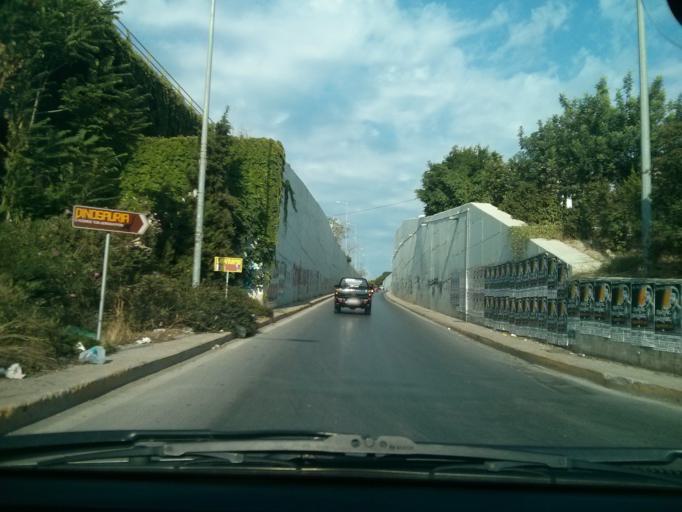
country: GR
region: Crete
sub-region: Nomos Irakleiou
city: Irakleion
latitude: 35.3204
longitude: 25.1439
